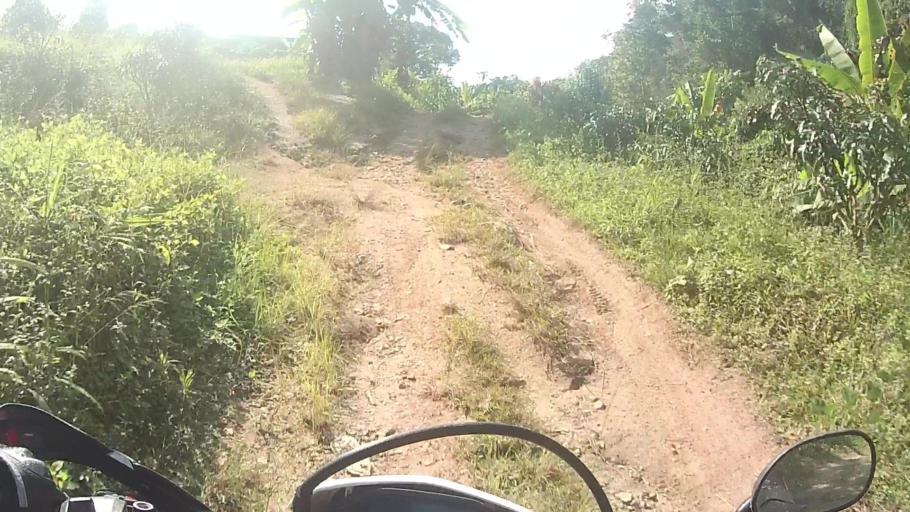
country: TH
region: Chiang Mai
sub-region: Amphoe Chiang Dao
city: Chiang Dao
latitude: 19.3547
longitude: 98.8207
